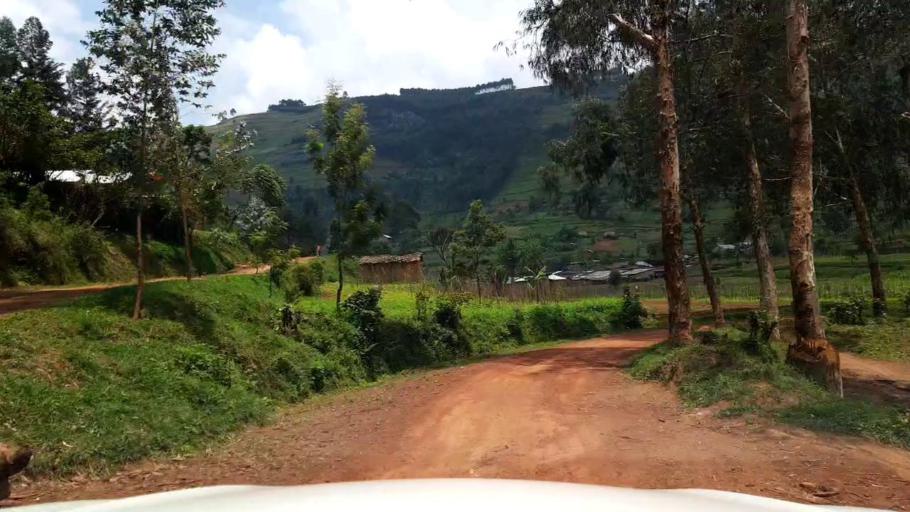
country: RW
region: Northern Province
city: Byumba
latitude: -1.4795
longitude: 29.9078
